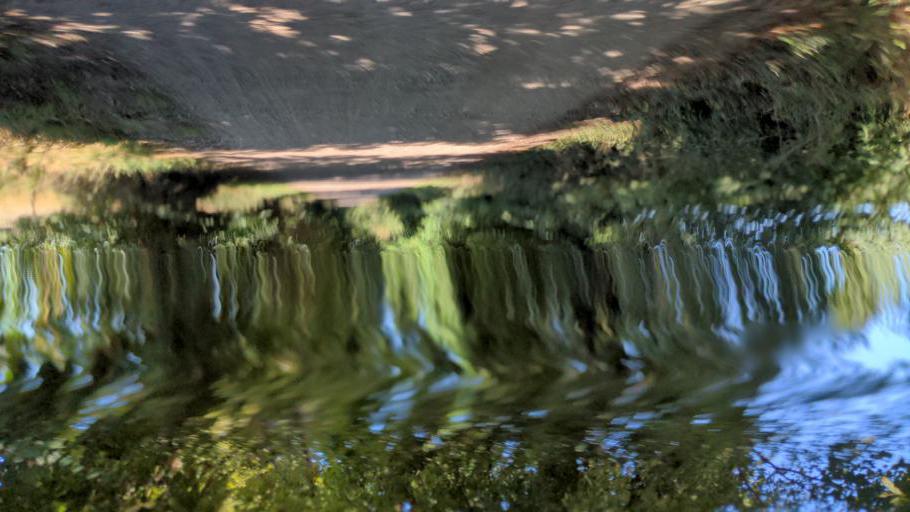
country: DE
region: Mecklenburg-Vorpommern
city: Klutz
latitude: 53.9809
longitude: 11.1714
